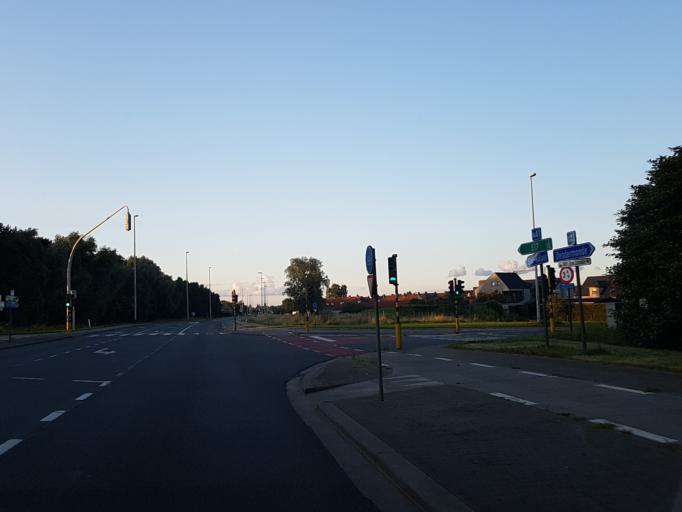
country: BE
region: Flanders
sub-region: Provincie Oost-Vlaanderen
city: Hamme
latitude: 51.0869
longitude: 4.1453
